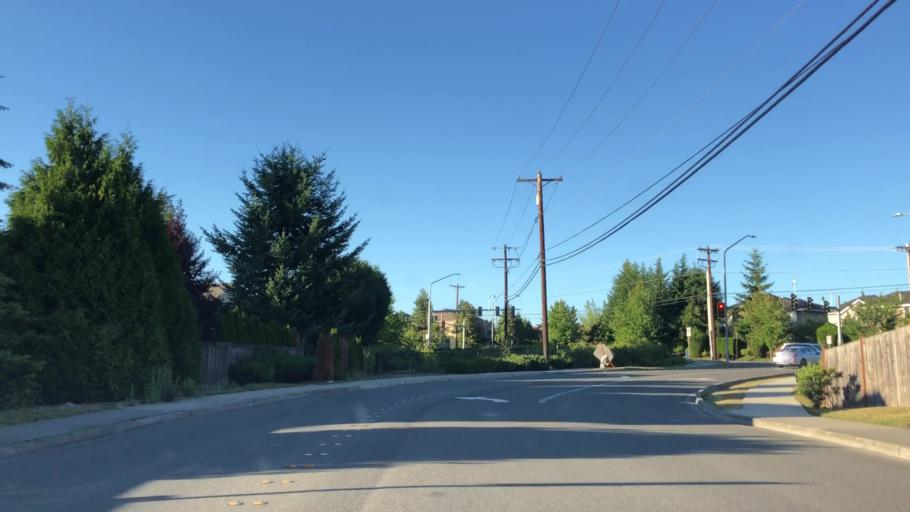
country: US
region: Washington
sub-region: Snohomish County
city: North Creek
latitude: 47.8261
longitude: -122.1869
